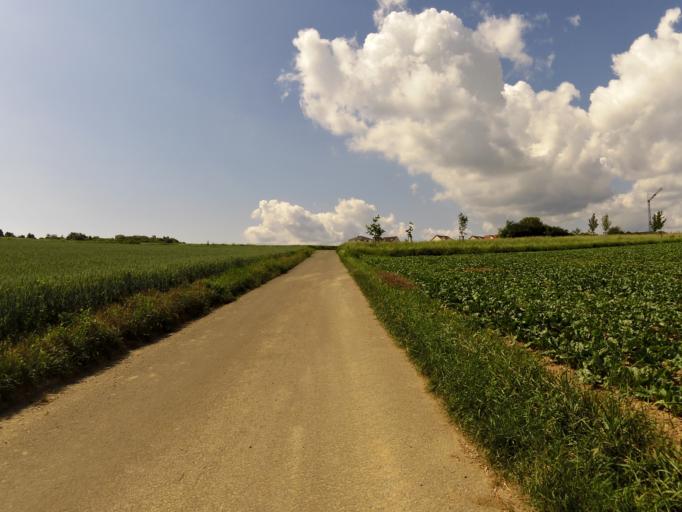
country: DE
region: Rheinland-Pfalz
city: Tiefenthal
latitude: 49.5435
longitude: 8.1116
